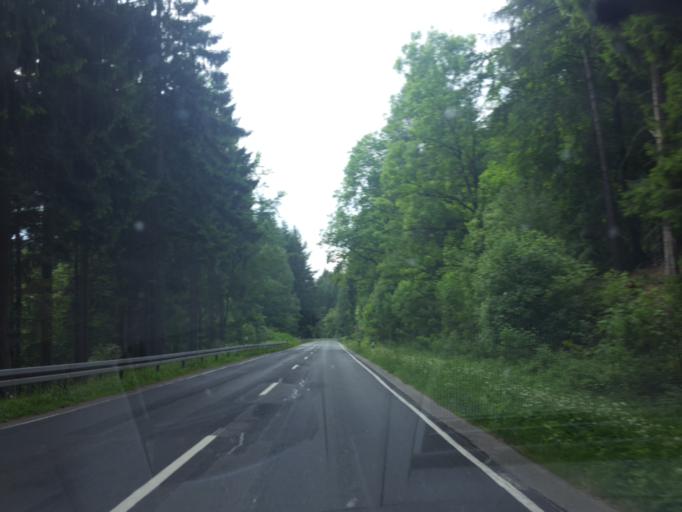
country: DE
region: Lower Saxony
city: Bad Grund
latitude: 51.8231
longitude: 10.2233
